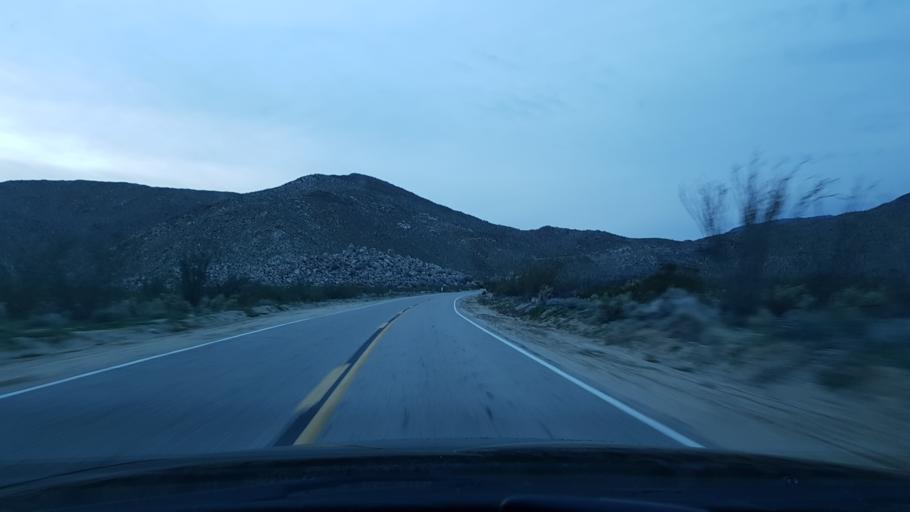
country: US
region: California
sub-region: San Diego County
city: Pine Valley
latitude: 32.9738
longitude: -116.4092
